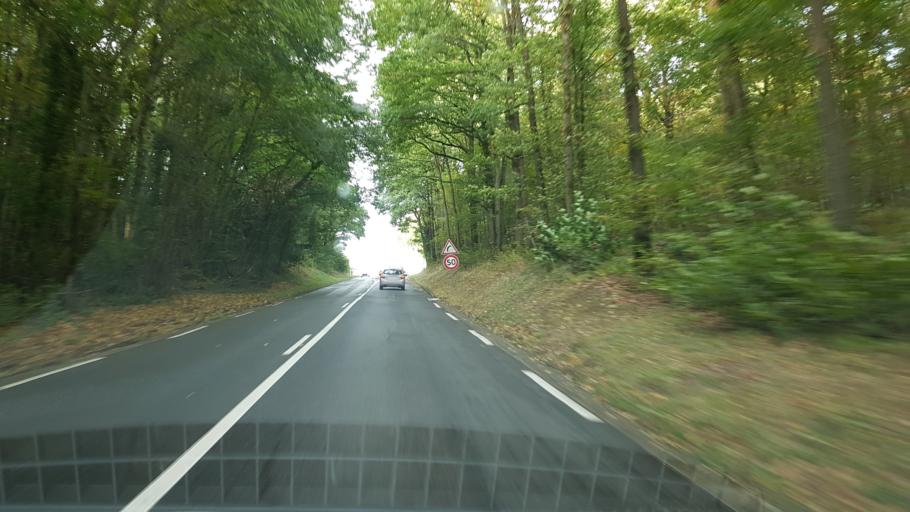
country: FR
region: Ile-de-France
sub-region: Departement de l'Essonne
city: Fontenay-les-Briis
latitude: 48.6309
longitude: 2.1762
